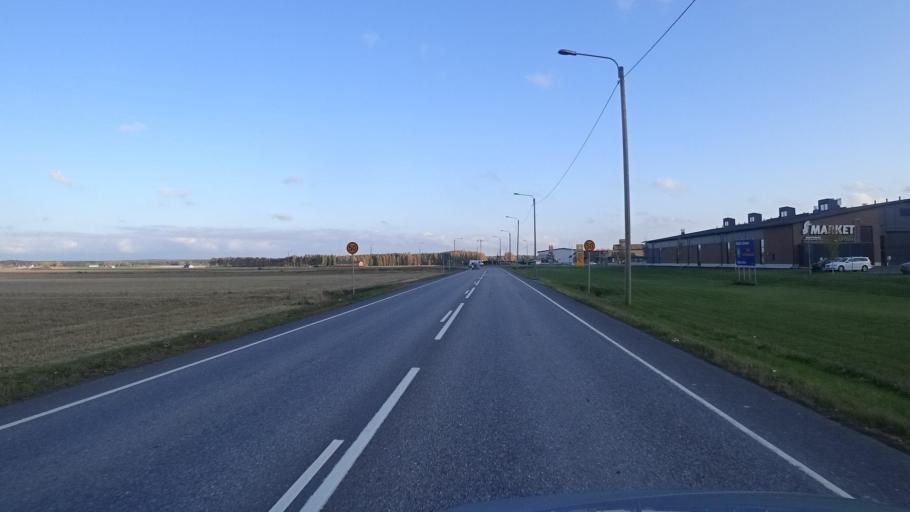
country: FI
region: Satakunta
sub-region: Rauma
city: Saekylae
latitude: 61.0476
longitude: 22.3555
